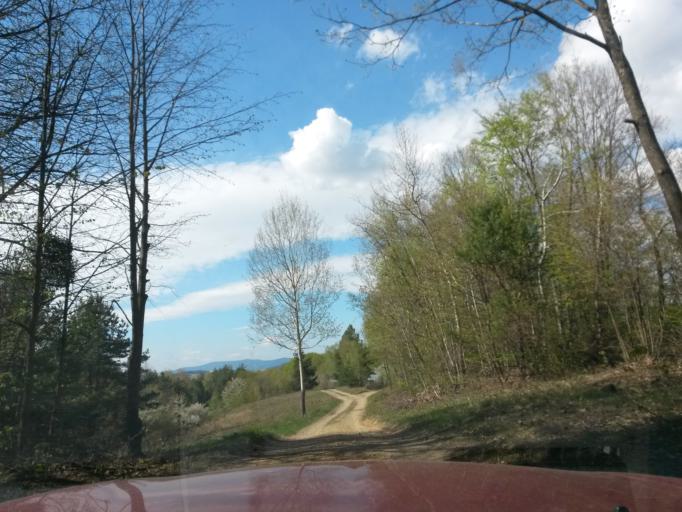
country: SK
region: Presovsky
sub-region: Okres Presov
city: Presov
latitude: 48.9376
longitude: 21.1222
